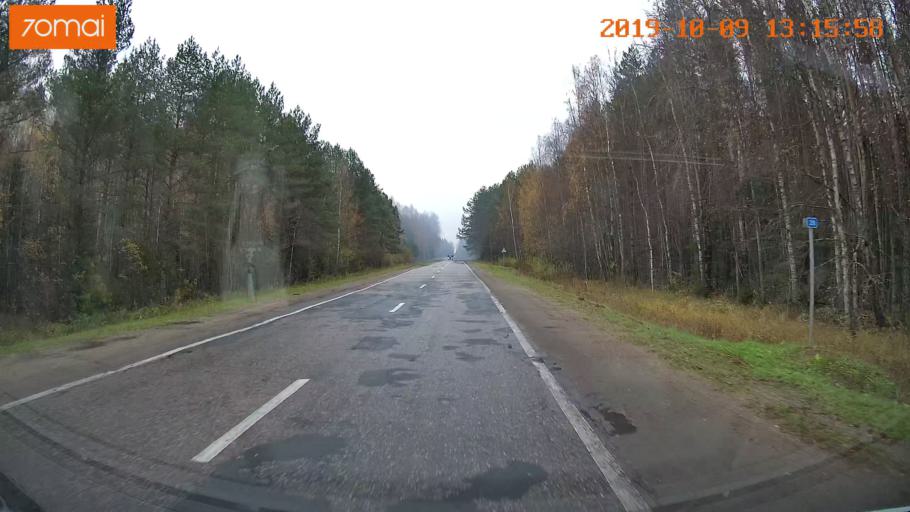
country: RU
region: Jaroslavl
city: Lyubim
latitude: 58.3643
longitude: 40.7597
